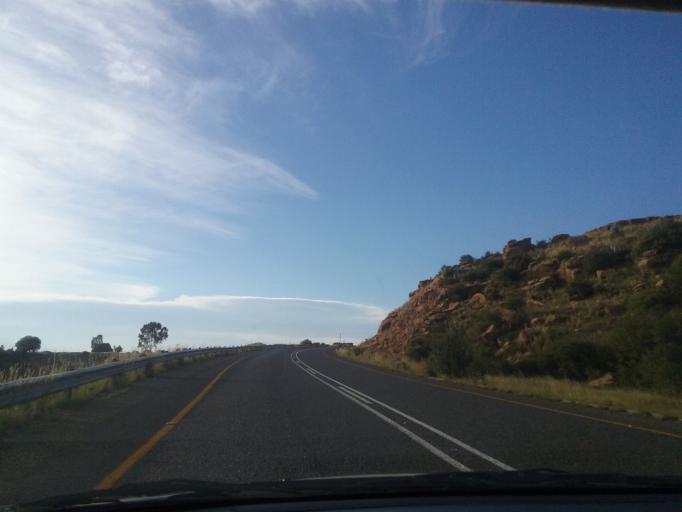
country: LS
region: Mohale's Hoek District
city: Mohale's Hoek
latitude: -30.2382
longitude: 27.4343
